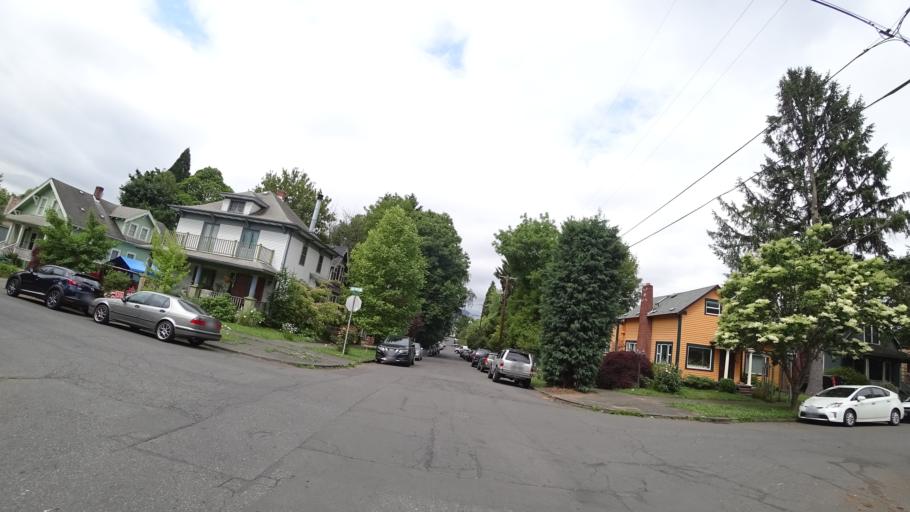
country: US
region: Oregon
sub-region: Multnomah County
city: Portland
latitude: 45.4992
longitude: -122.6406
